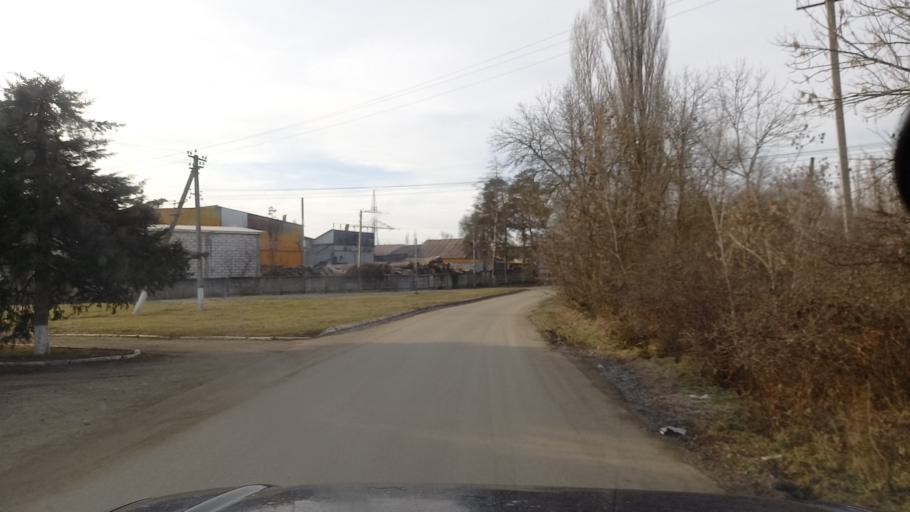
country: RU
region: Krasnodarskiy
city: Apsheronsk
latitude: 44.4828
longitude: 39.7315
